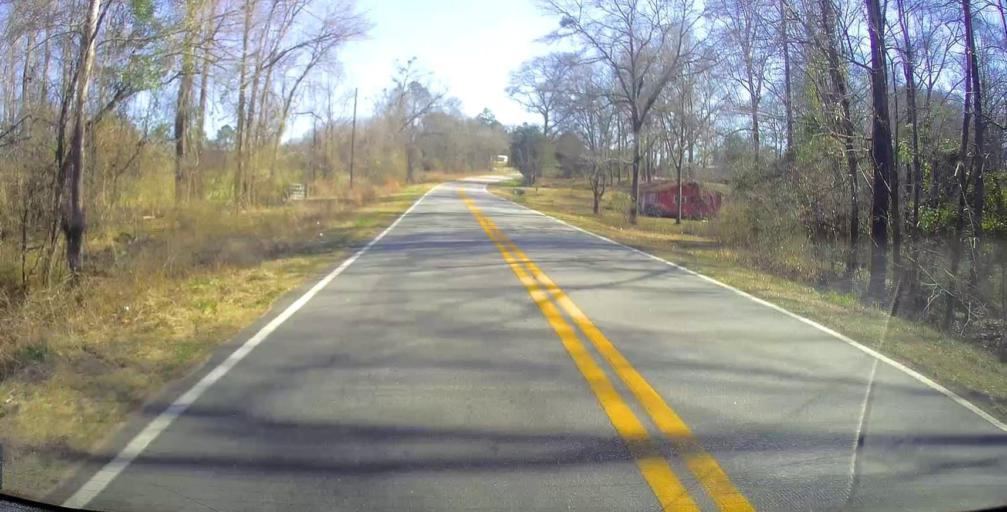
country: US
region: Georgia
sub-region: Crawford County
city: Knoxville
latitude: 32.7158
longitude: -83.9968
